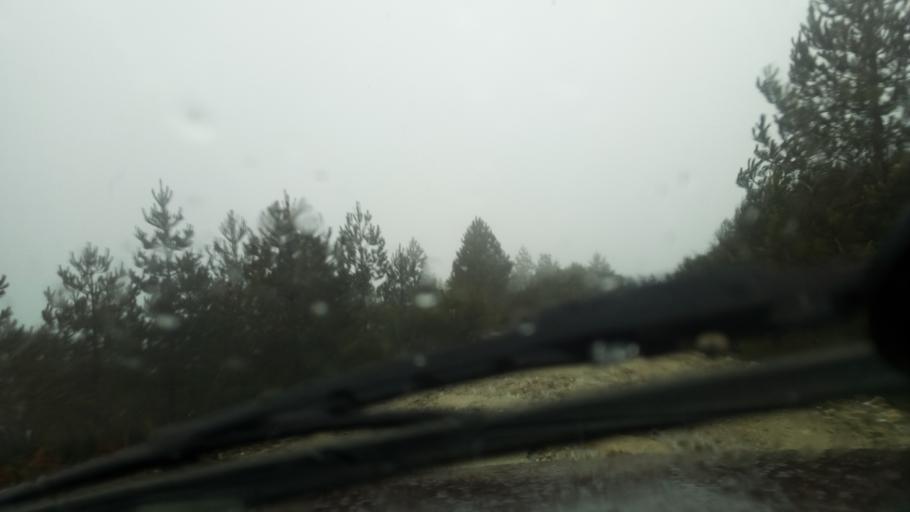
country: PT
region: Guarda
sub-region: Celorico da Beira
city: Celorico da Beira
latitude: 40.5281
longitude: -7.4502
